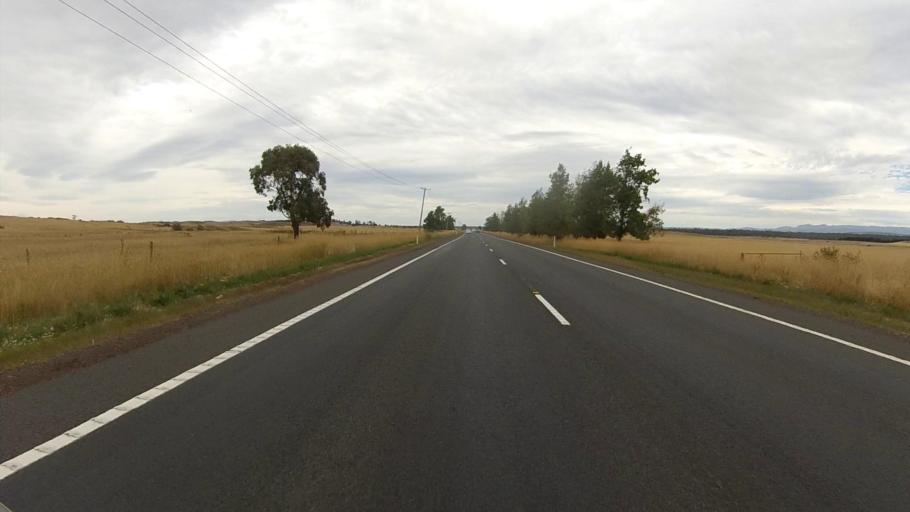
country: AU
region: Tasmania
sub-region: Northern Midlands
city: Evandale
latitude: -41.8924
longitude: 147.4714
